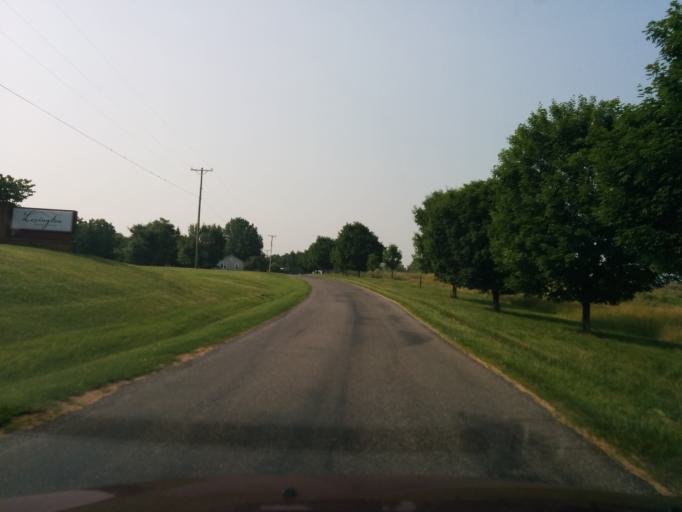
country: US
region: Virginia
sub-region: City of Lexington
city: Lexington
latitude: 37.7715
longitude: -79.4377
